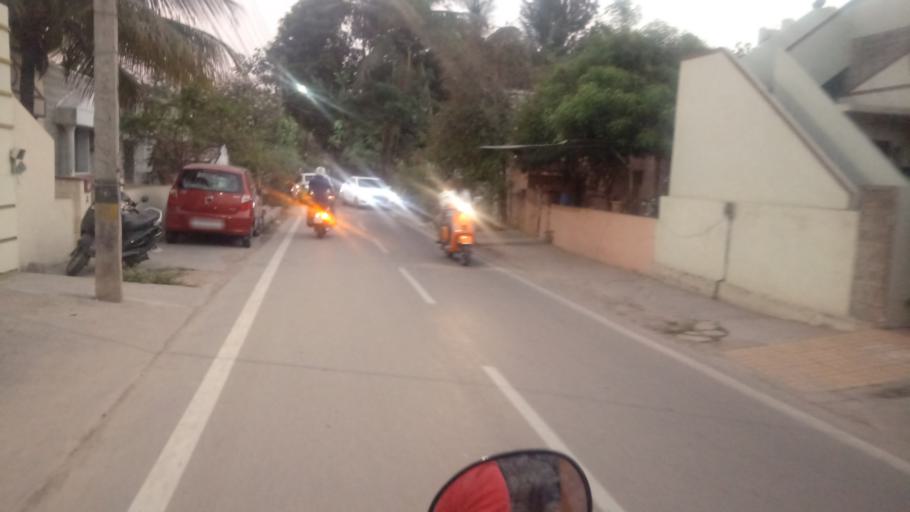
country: IN
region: Telangana
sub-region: Rangareddi
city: Kukatpalli
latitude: 17.5020
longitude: 78.3983
